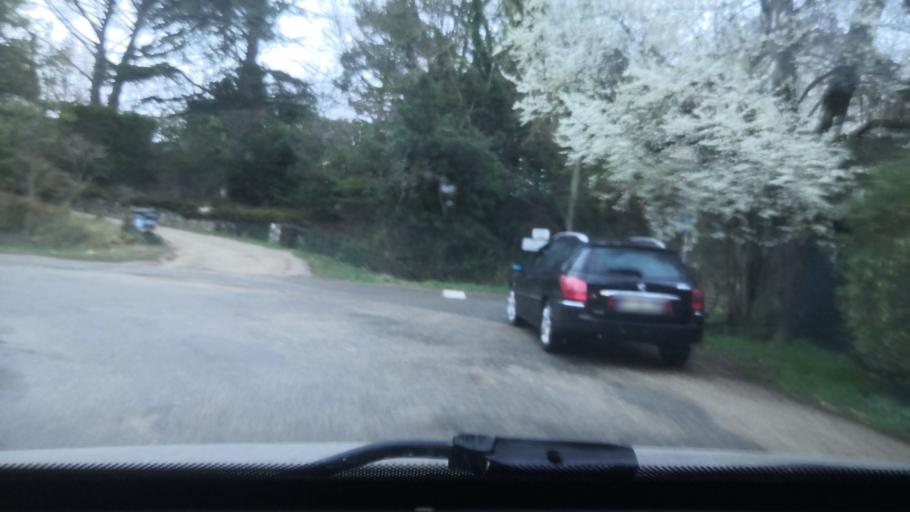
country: FR
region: Rhone-Alpes
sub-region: Departement de la Drome
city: Dieulefit
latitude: 44.5177
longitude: 5.0583
